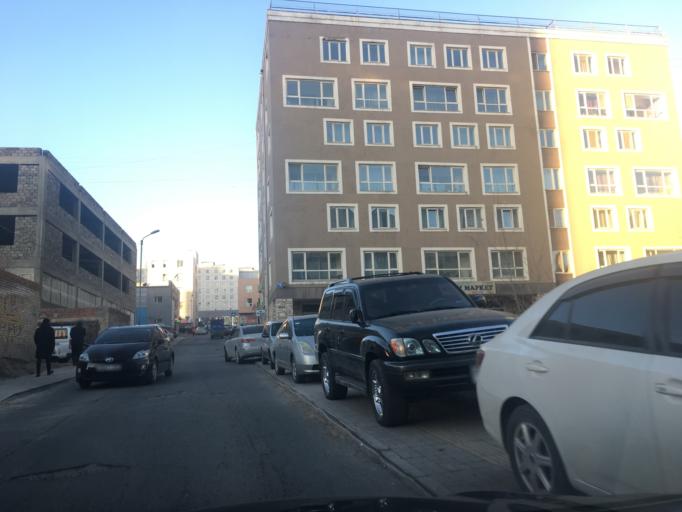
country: MN
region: Ulaanbaatar
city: Ulaanbaatar
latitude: 47.9212
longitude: 106.8817
